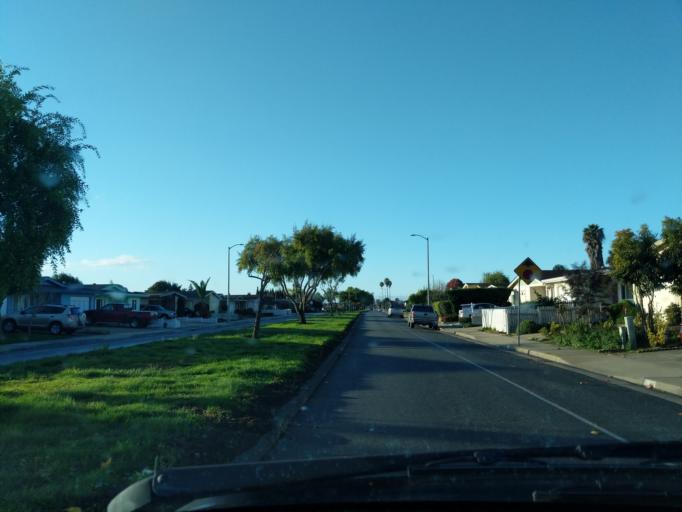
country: US
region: California
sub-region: Monterey County
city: Pajaro
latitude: 36.9182
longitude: -121.7417
